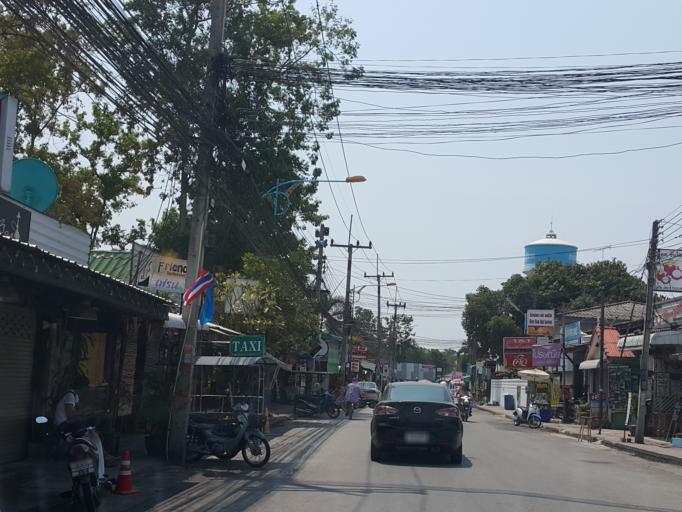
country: TH
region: Kanchanaburi
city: Kanchanaburi
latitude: 14.0330
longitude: 99.5209
